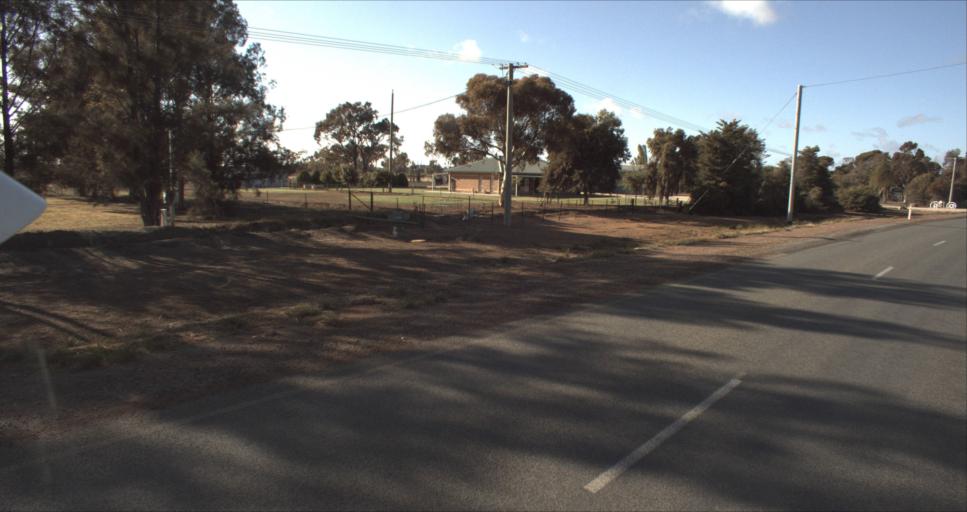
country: AU
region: New South Wales
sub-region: Leeton
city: Leeton
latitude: -34.5367
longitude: 146.3882
